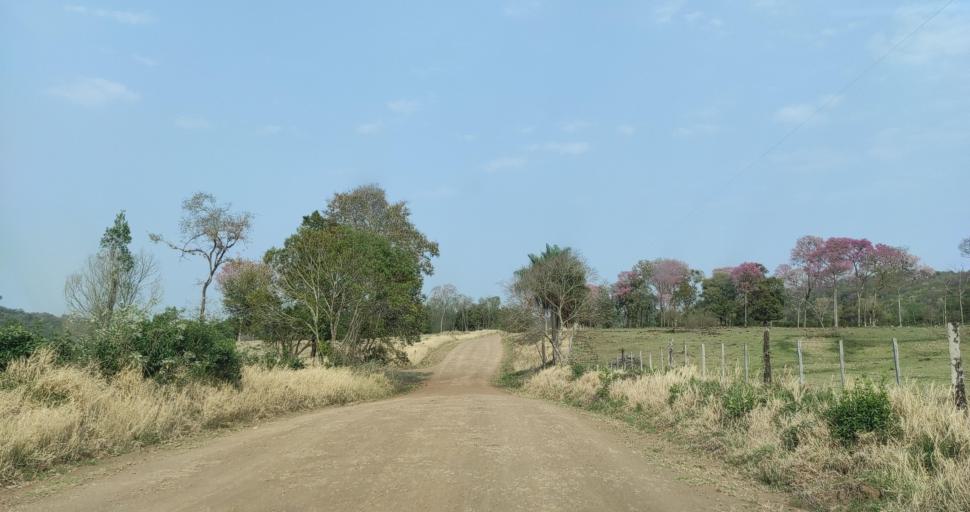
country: AR
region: Misiones
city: Cerro Azul
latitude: -27.6163
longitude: -55.5633
